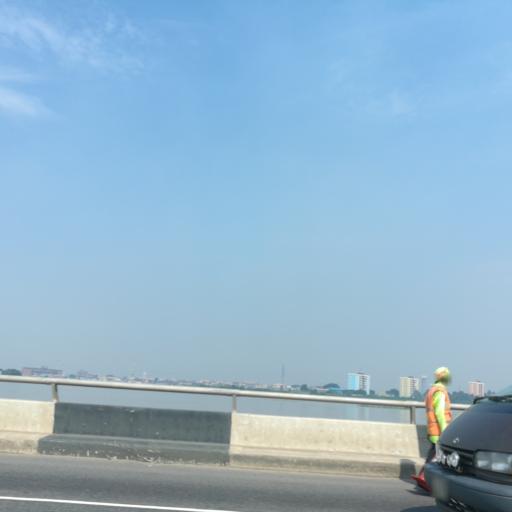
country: NG
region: Lagos
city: Makoko
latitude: 6.5034
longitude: 3.4022
